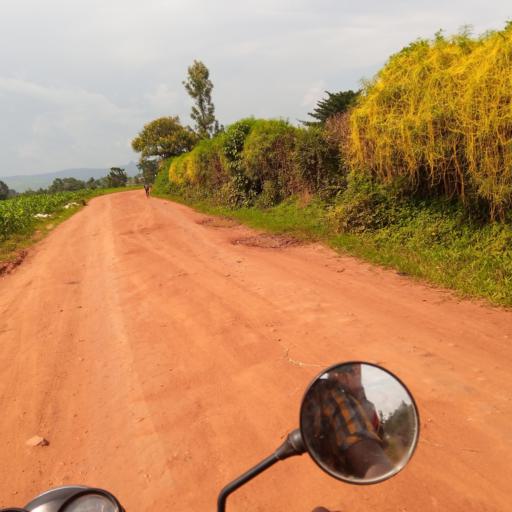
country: UG
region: Eastern Region
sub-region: Mbale District
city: Mbale
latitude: 1.0941
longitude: 34.1877
